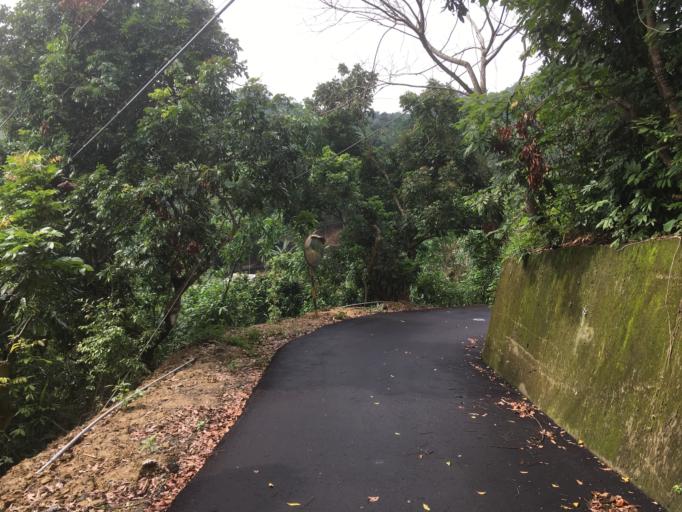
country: TW
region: Taiwan
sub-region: Taichung City
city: Taichung
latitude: 24.1716
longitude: 120.7772
